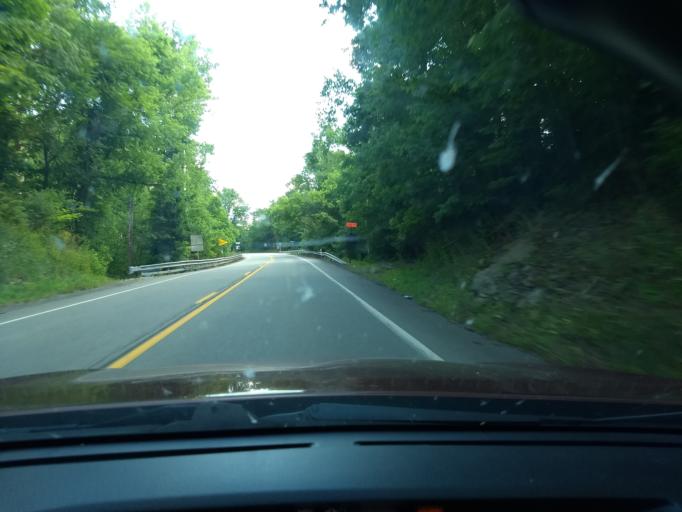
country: US
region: Pennsylvania
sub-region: Westmoreland County
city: Irwin
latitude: 40.3511
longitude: -79.7321
